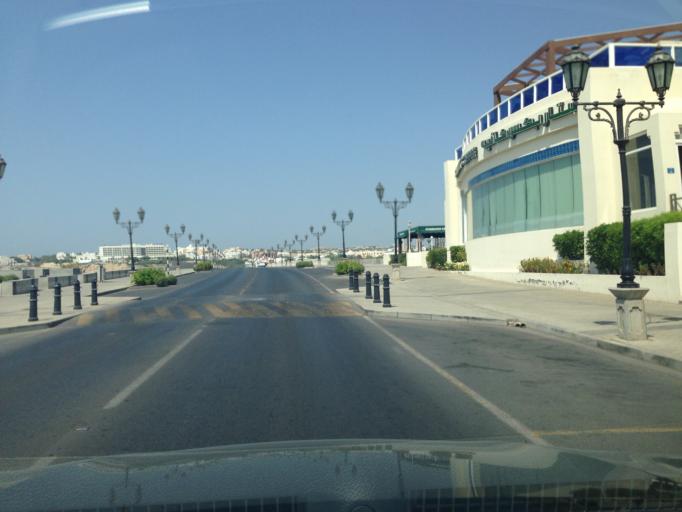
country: OM
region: Muhafazat Masqat
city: Bawshar
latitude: 23.6226
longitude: 58.4750
